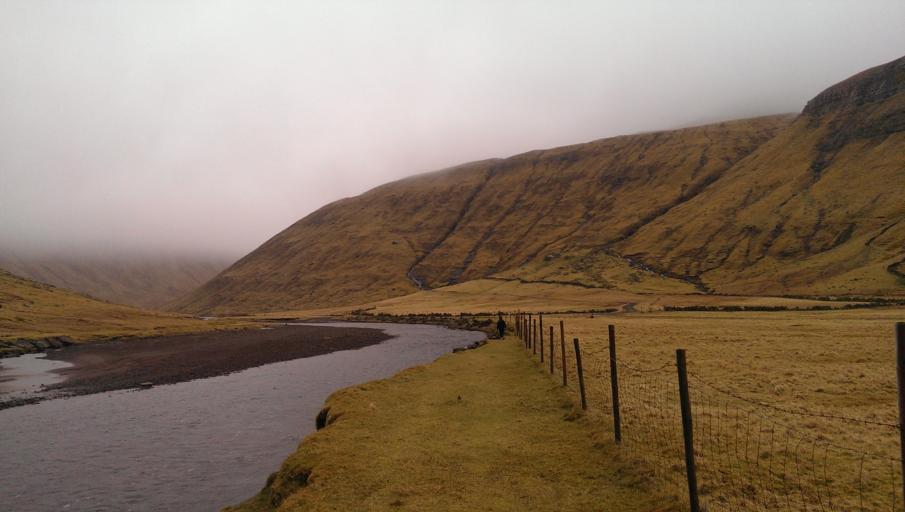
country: FO
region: Streymoy
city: Kollafjordhur
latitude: 62.1329
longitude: -7.0236
